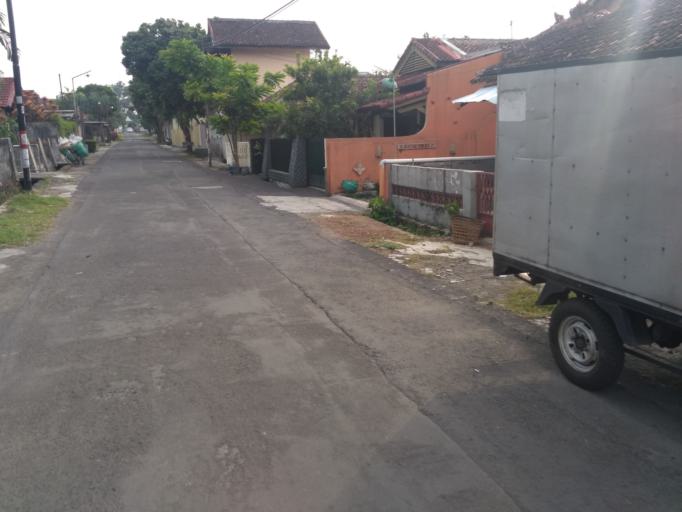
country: ID
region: Daerah Istimewa Yogyakarta
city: Melati
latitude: -7.7363
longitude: 110.3883
